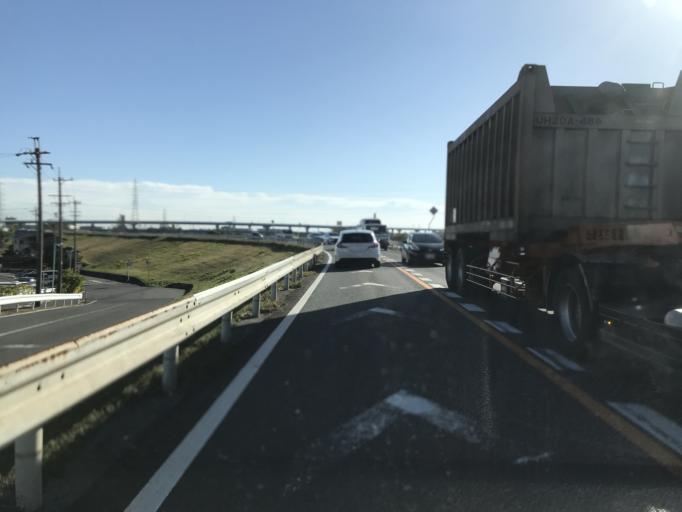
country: JP
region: Aichi
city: Kanie
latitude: 35.1647
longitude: 136.8356
